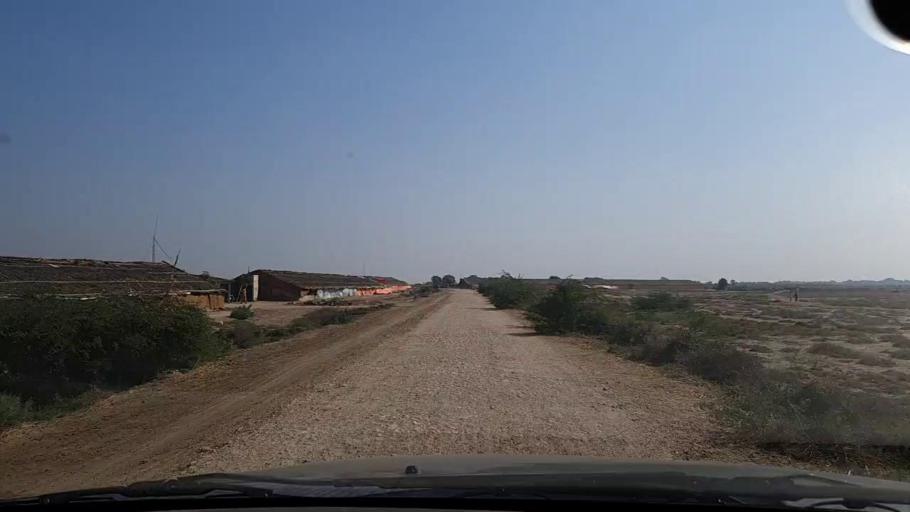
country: PK
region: Sindh
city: Chuhar Jamali
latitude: 24.4200
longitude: 67.8252
